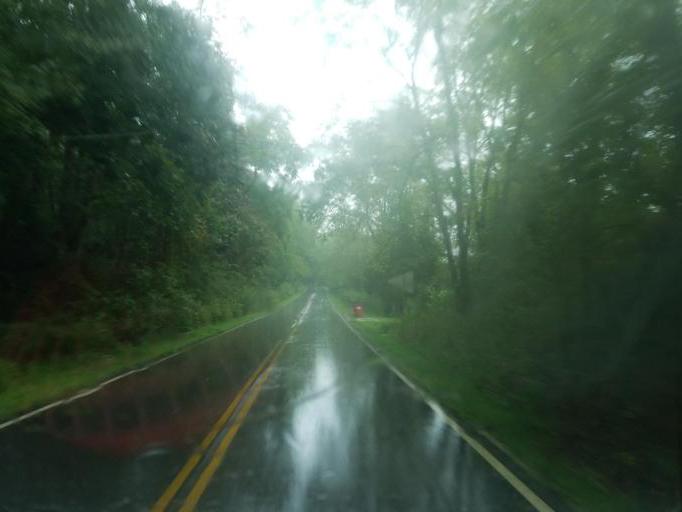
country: US
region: Kentucky
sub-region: Greenup County
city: Greenup
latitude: 38.4979
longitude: -82.9712
